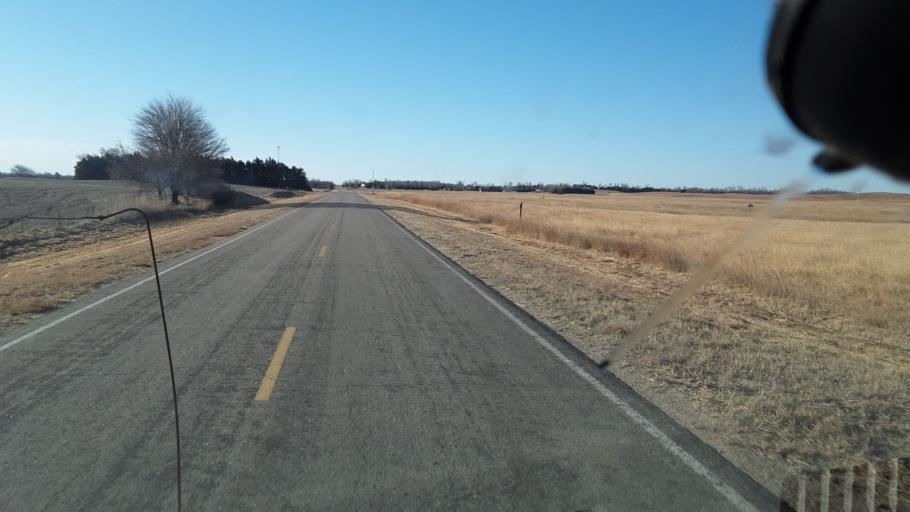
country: US
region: Kansas
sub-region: Barton County
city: Ellinwood
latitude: 38.3076
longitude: -98.6643
